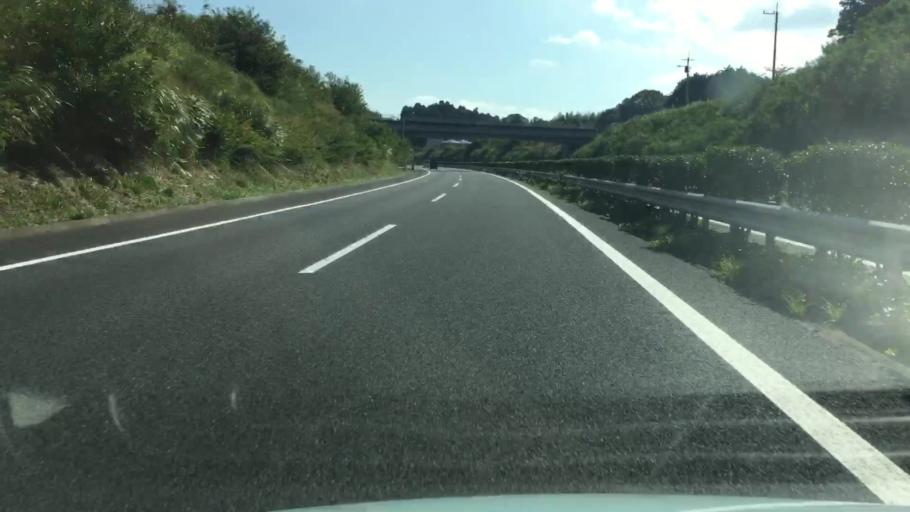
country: JP
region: Ibaraki
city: Tomobe
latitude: 36.3162
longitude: 140.3163
